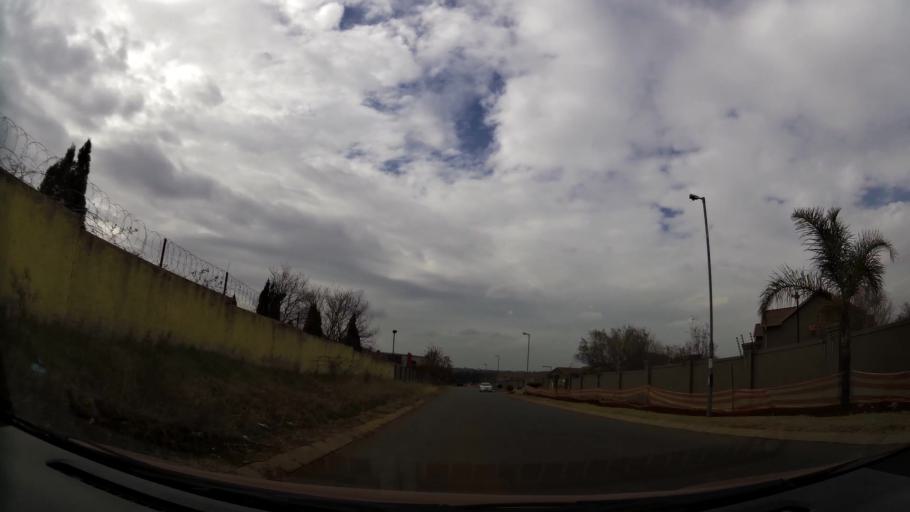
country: ZA
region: Gauteng
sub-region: West Rand District Municipality
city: Muldersdriseloop
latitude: -26.0905
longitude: 27.8754
